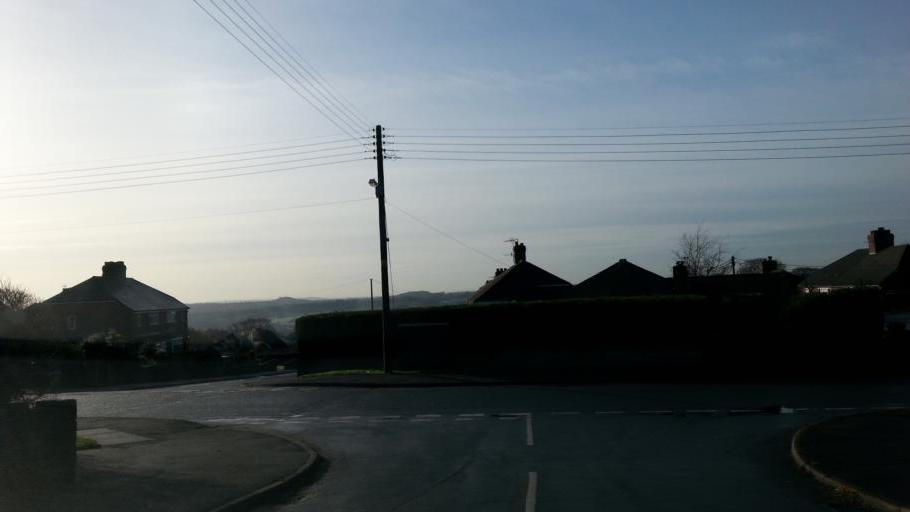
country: GB
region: England
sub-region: Staffordshire
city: Biddulph
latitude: 53.0747
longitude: -2.1375
